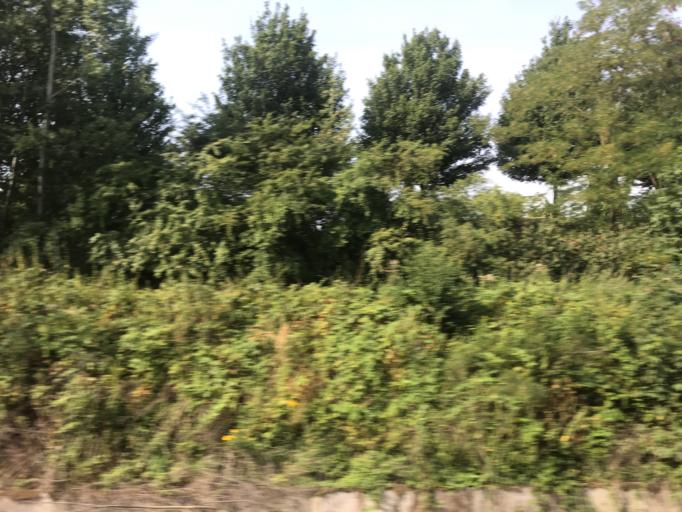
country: CZ
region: Praha
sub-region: Praha 14
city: Dolni Pocernice
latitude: 50.0521
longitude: 14.5591
